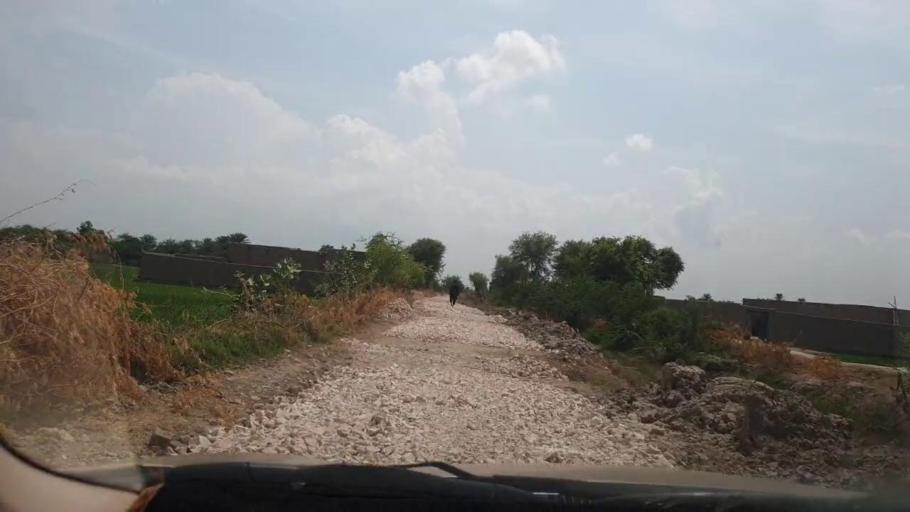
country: PK
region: Sindh
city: Larkana
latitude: 27.5643
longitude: 68.1095
